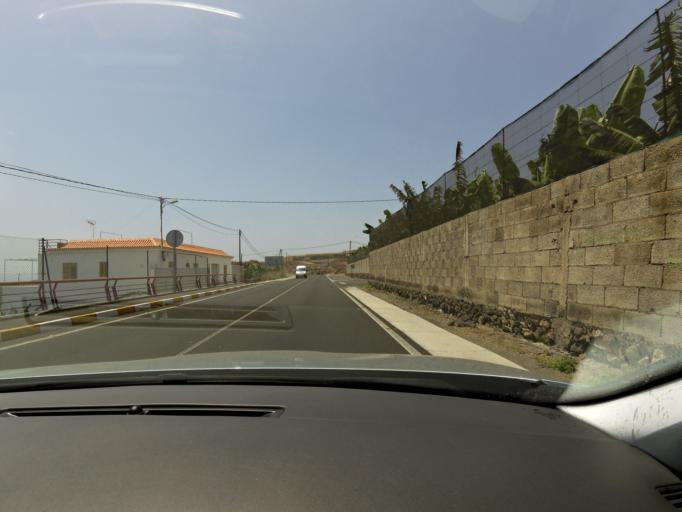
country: ES
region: Canary Islands
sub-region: Provincia de Santa Cruz de Tenerife
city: Adeje
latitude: 28.1326
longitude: -16.7642
